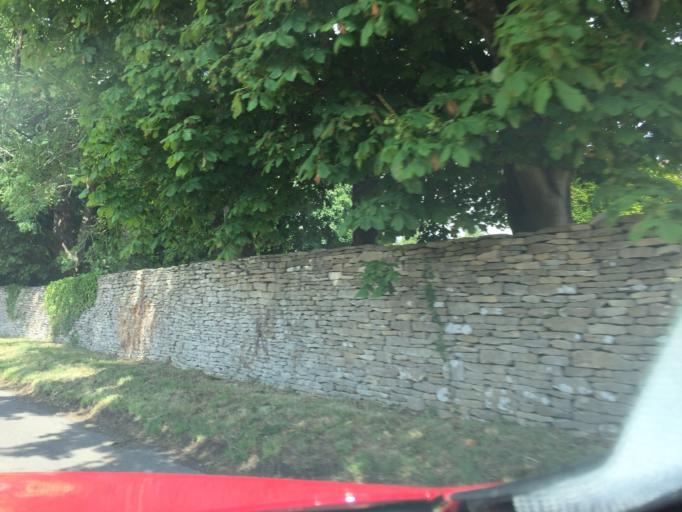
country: GB
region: England
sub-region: Gloucestershire
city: Chalford
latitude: 51.6844
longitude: -2.1429
